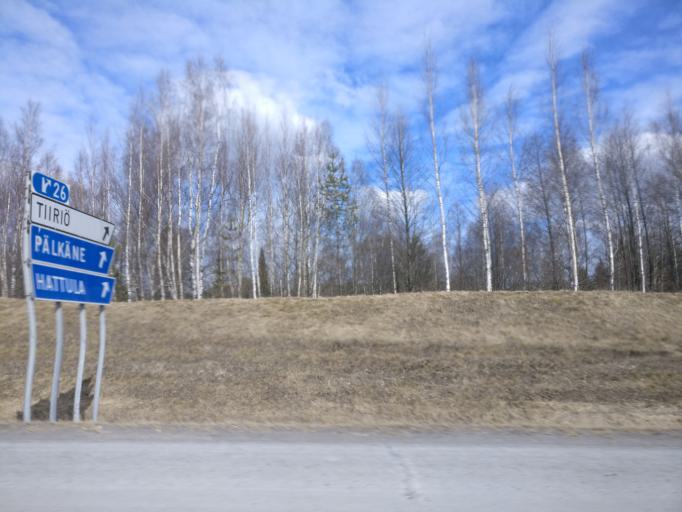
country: FI
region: Haeme
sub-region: Haemeenlinna
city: Haemeenlinna
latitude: 61.0099
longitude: 24.4267
